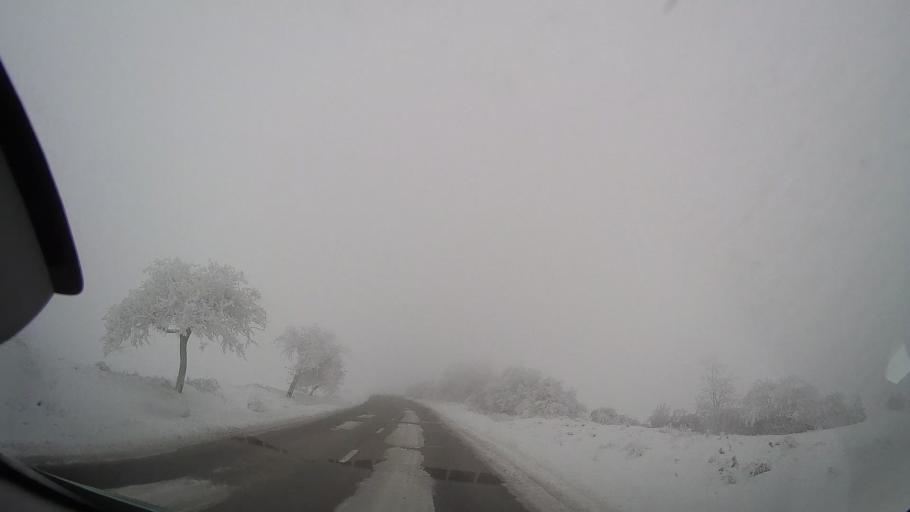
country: RO
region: Neamt
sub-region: Comuna Valea Ursului
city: Valea Ursului
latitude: 46.8220
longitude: 27.0635
